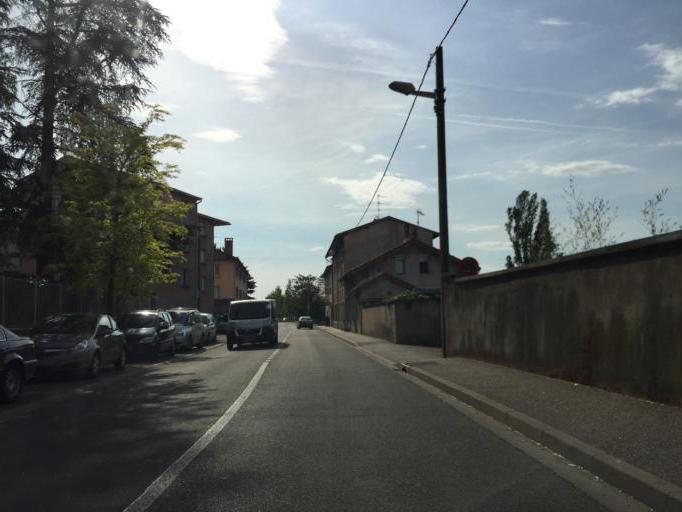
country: FR
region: Rhone-Alpes
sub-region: Departement de la Drome
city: Romans-sur-Isere
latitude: 45.0407
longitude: 5.0538
